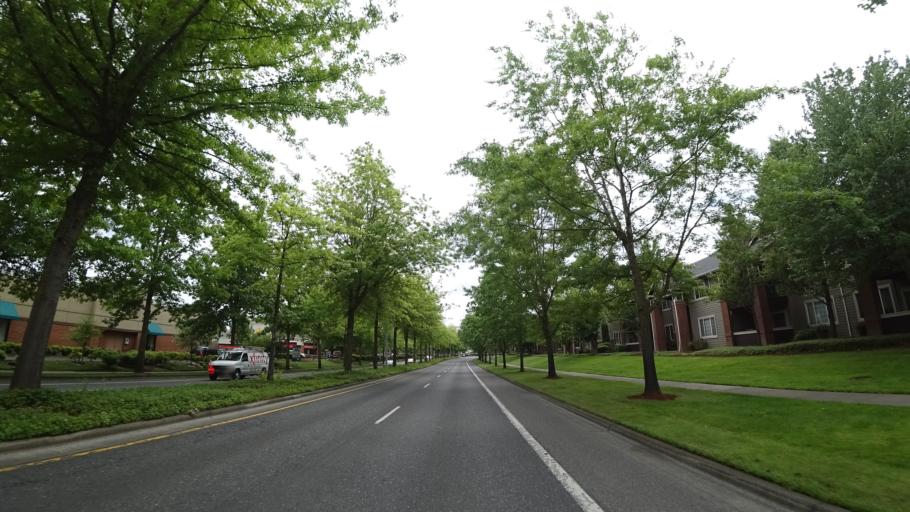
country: US
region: Oregon
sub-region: Washington County
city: Rockcreek
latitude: 45.5373
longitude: -122.9059
